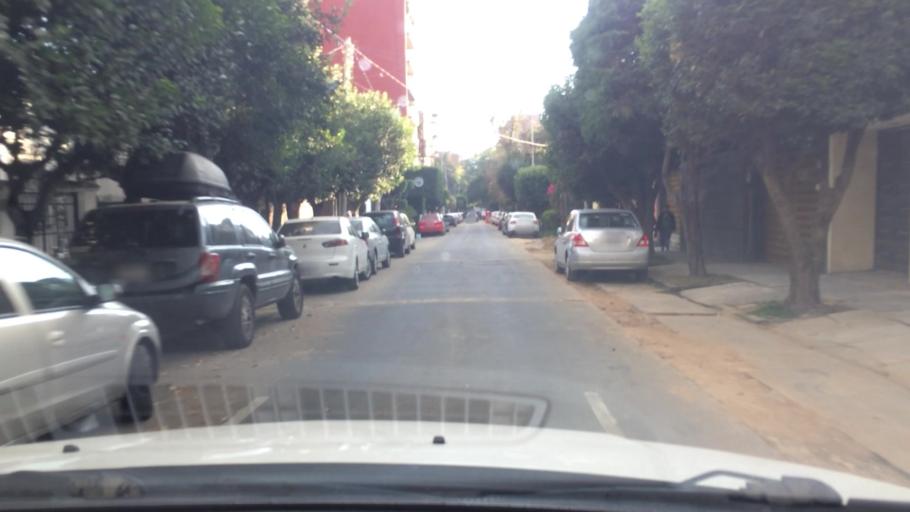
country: MX
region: Mexico City
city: Alvaro Obregon
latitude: 19.3600
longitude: -99.1886
